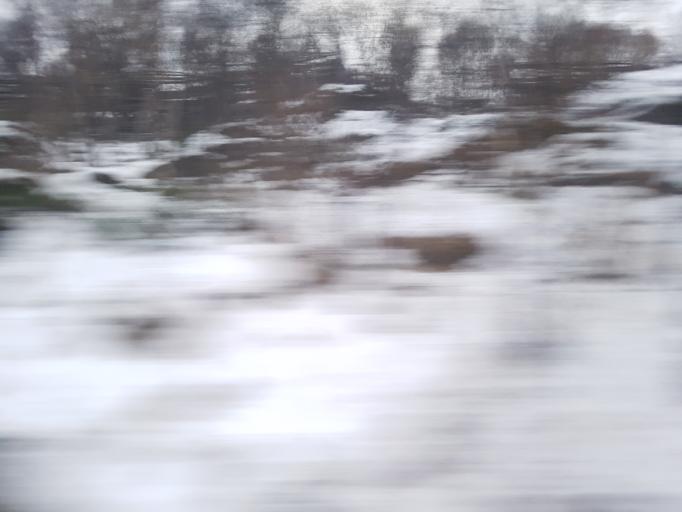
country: NO
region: Sor-Trondelag
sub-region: Oppdal
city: Oppdal
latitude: 62.2864
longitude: 9.5969
